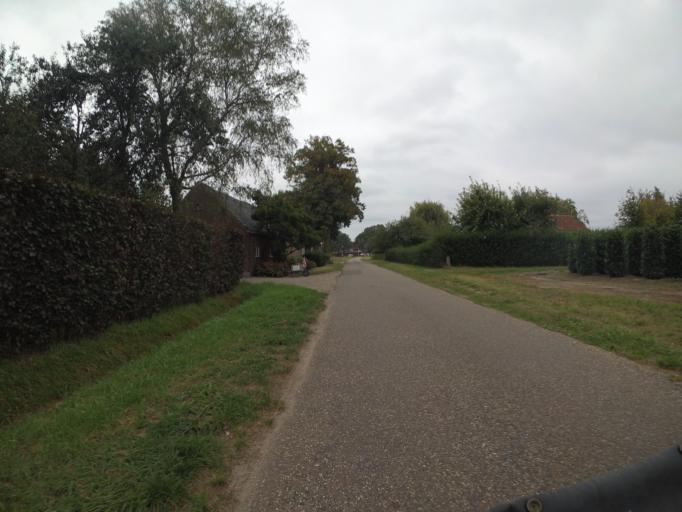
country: NL
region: North Brabant
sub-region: Gemeente Oisterwijk
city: Oisterwijk
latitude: 51.6035
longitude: 5.1646
